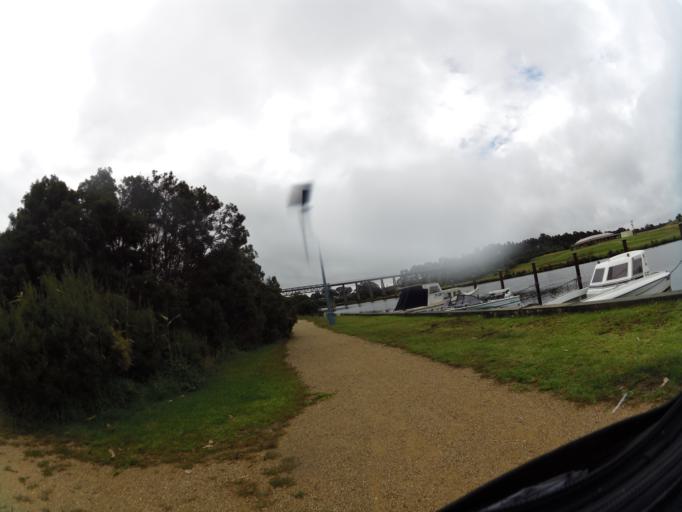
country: AU
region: Victoria
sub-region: East Gippsland
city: Bairnsdale
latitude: -37.8150
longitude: 147.7398
